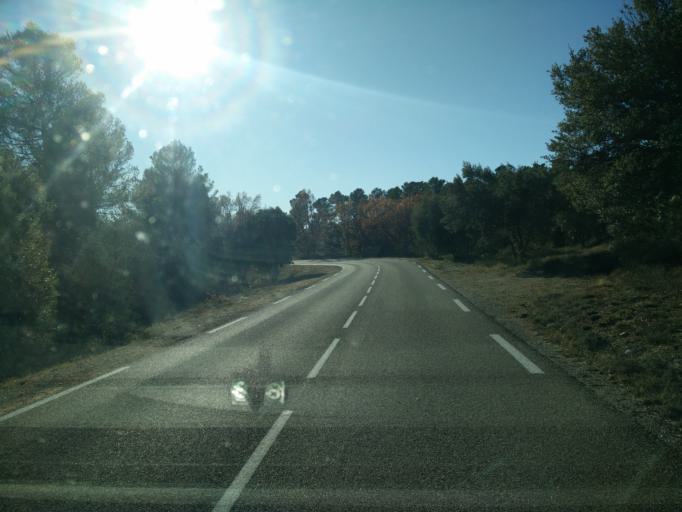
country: FR
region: Provence-Alpes-Cote d'Azur
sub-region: Departement du Var
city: Salernes
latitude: 43.5842
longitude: 6.2265
